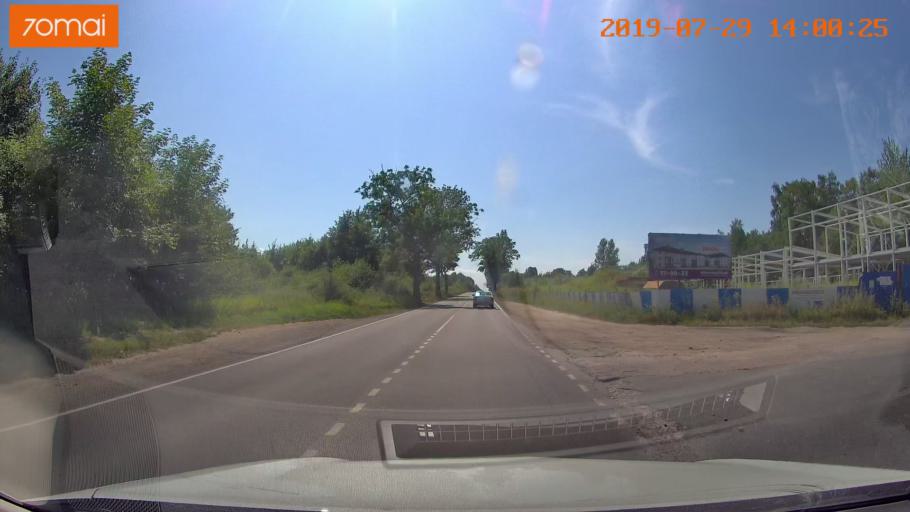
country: RU
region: Kaliningrad
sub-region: Gorod Kaliningrad
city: Baltiysk
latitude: 54.6786
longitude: 19.9280
